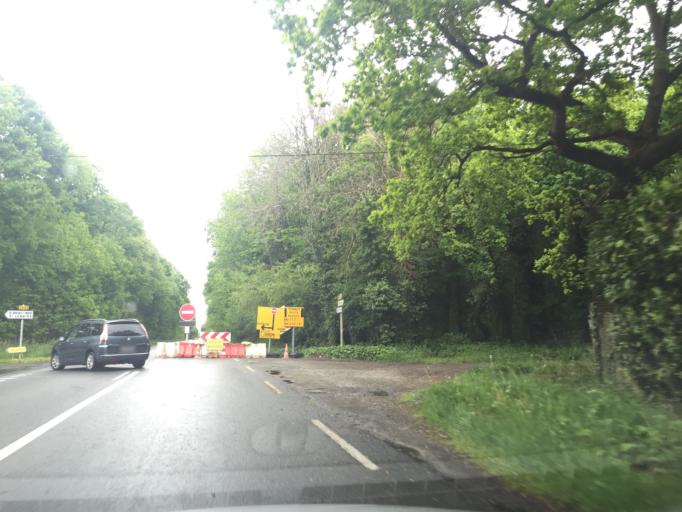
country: FR
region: Brittany
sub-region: Departement d'Ille-et-Vilaine
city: Pleurtuit
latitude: 48.5961
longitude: -2.0953
